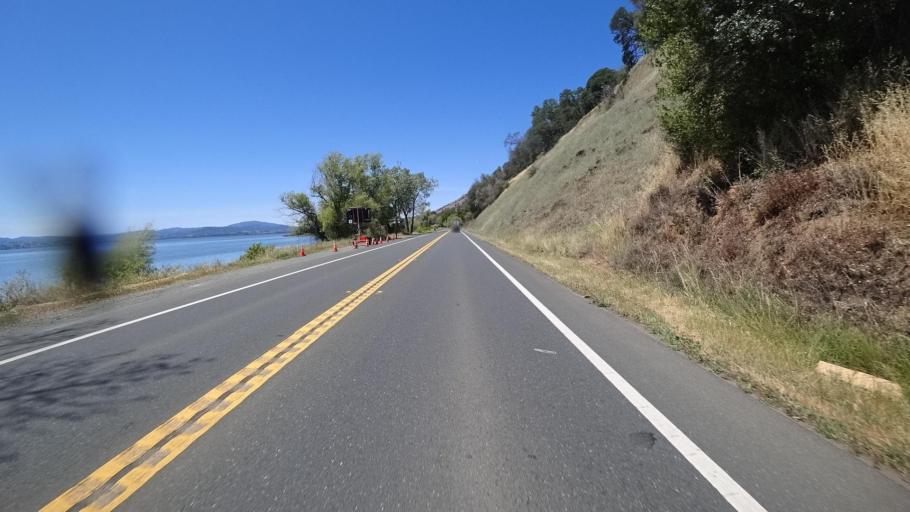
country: US
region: California
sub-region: Lake County
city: Lucerne
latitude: 39.1009
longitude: -122.8065
